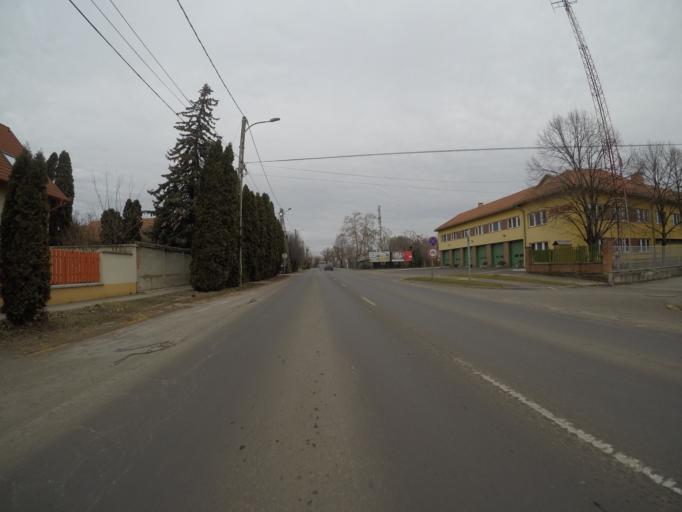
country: HU
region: Jasz-Nagykun-Szolnok
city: Jaszbereny
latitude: 47.5037
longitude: 19.9270
